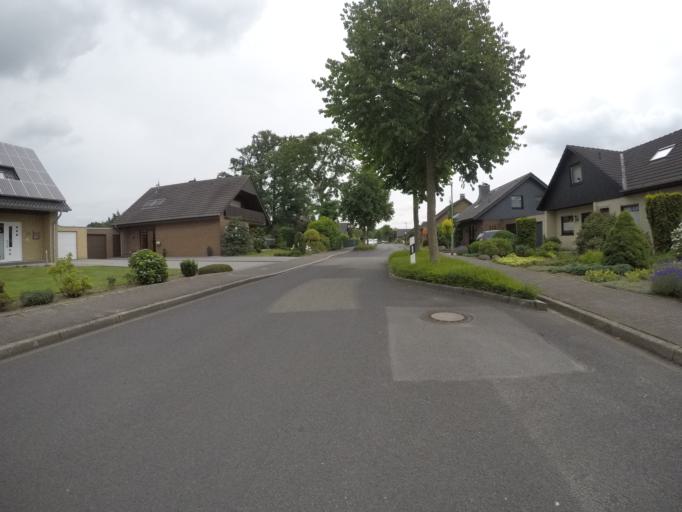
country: DE
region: North Rhine-Westphalia
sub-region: Regierungsbezirk Munster
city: Isselburg
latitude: 51.8528
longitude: 6.4265
